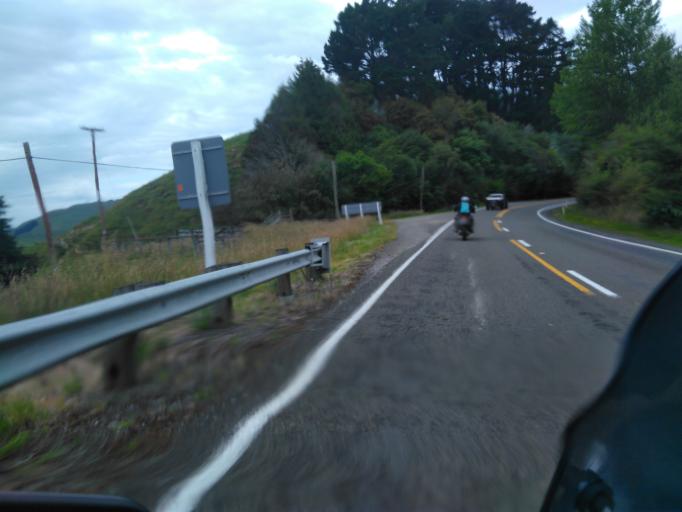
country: NZ
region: Bay of Plenty
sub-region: Opotiki District
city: Opotiki
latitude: -38.3938
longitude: 177.5611
